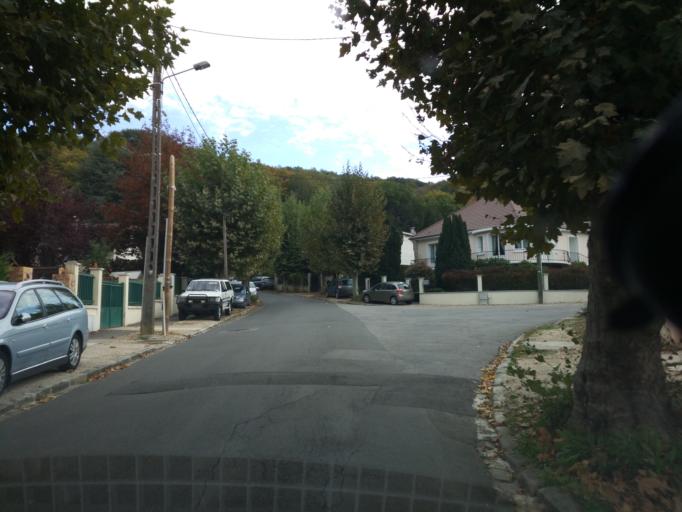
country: FR
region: Ile-de-France
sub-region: Departement des Yvelines
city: Saint-Remy-les-Chevreuse
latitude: 48.6966
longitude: 2.0653
